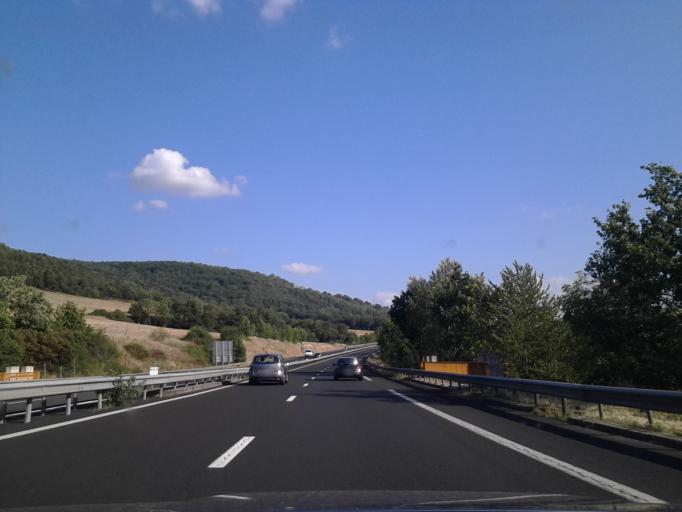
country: FR
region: Auvergne
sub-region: Departement du Cantal
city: Massiac
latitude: 45.2634
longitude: 3.2004
